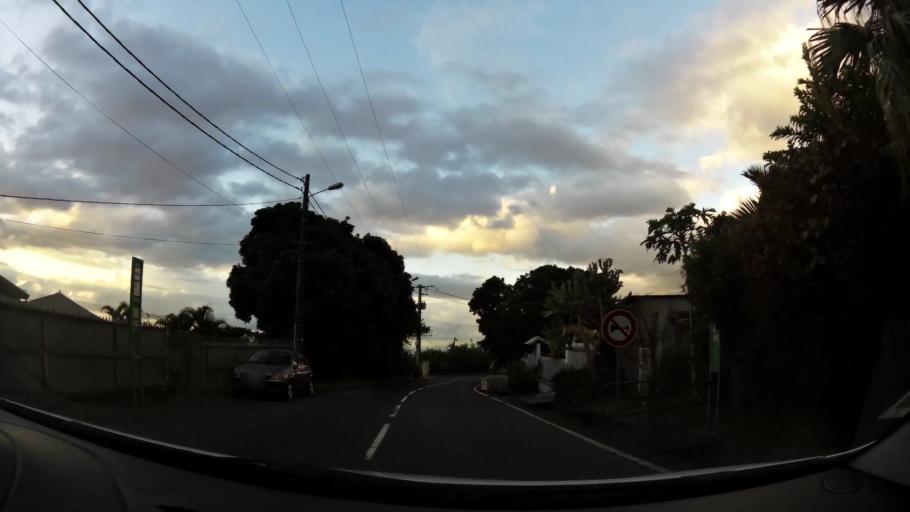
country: RE
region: Reunion
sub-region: Reunion
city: Saint-Denis
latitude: -20.9126
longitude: 55.4617
